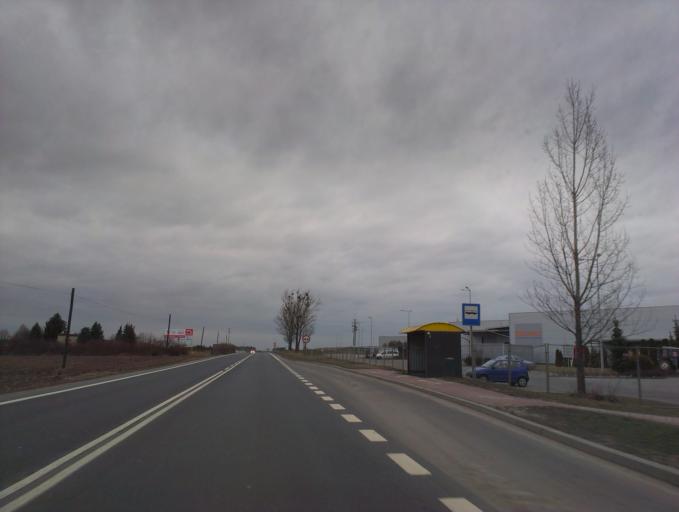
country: PL
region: Greater Poland Voivodeship
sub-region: Powiat poznanski
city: Zlotniki
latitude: 52.5078
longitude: 16.8349
